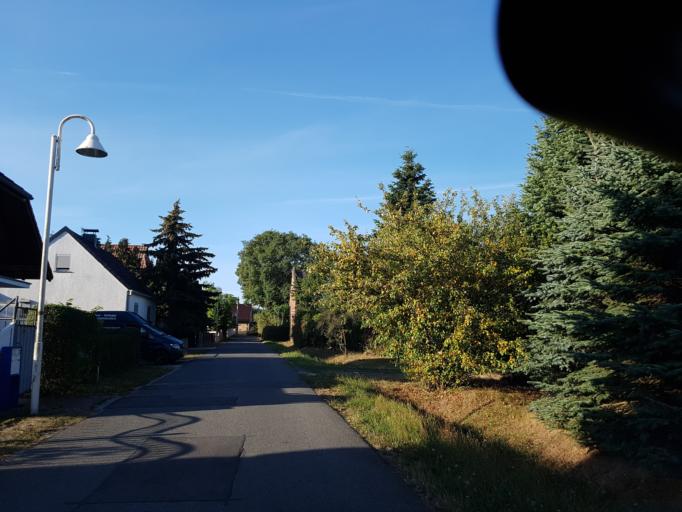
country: DE
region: Brandenburg
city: Plessa
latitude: 51.5315
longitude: 13.6347
